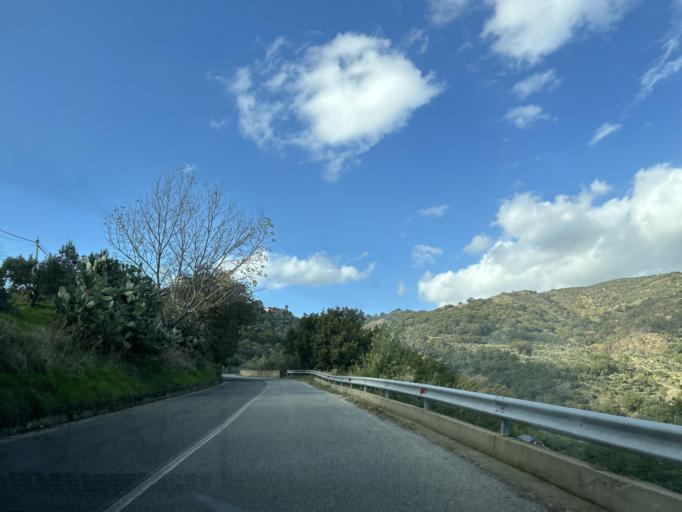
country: IT
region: Calabria
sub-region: Provincia di Catanzaro
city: Montepaone
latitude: 38.7221
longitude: 16.5069
